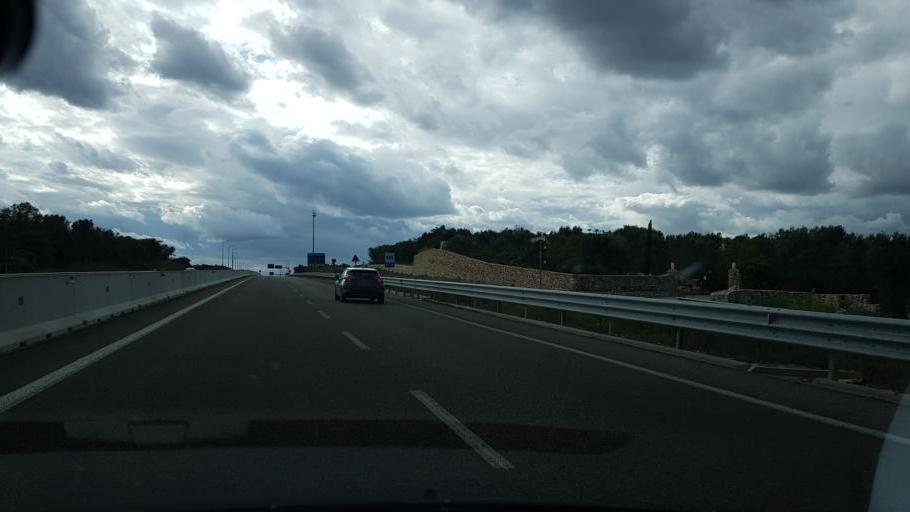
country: IT
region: Apulia
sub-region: Provincia di Lecce
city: Palmariggi
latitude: 40.1352
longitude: 18.4034
